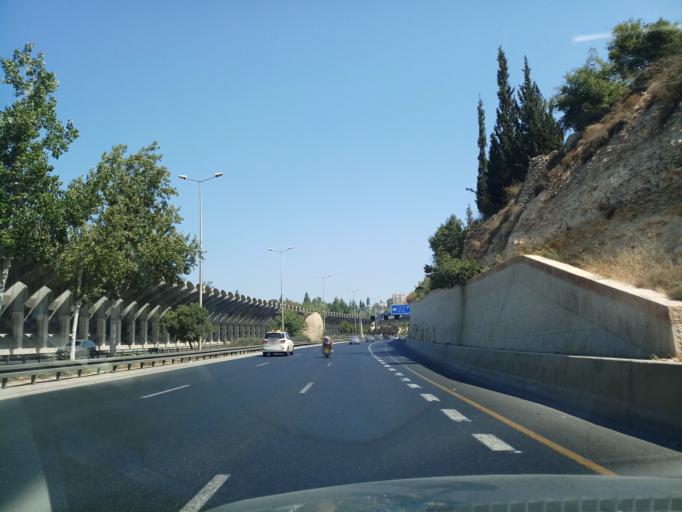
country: IL
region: Jerusalem
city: Jerusalem
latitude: 31.7755
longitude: 35.1940
